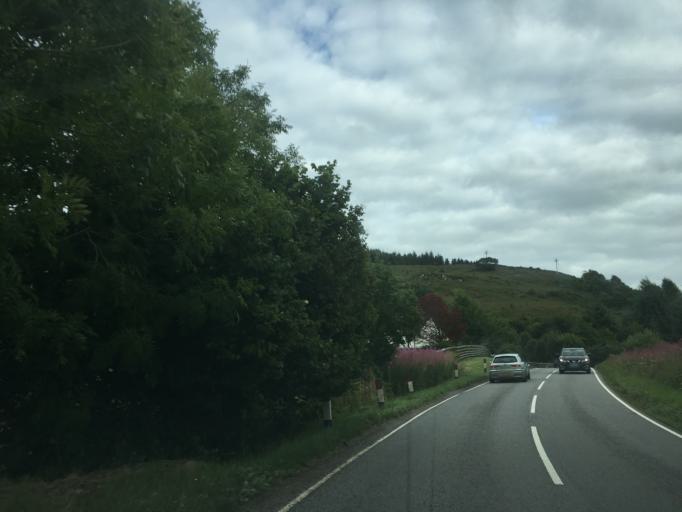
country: GB
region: Scotland
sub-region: Argyll and Bute
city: Oban
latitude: 56.3297
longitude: -5.5044
